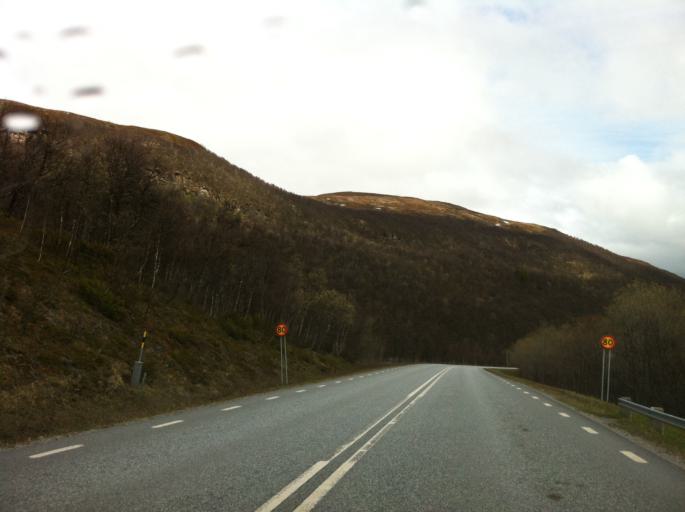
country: NO
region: Sor-Trondelag
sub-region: Tydal
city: Aas
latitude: 62.5709
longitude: 12.2343
